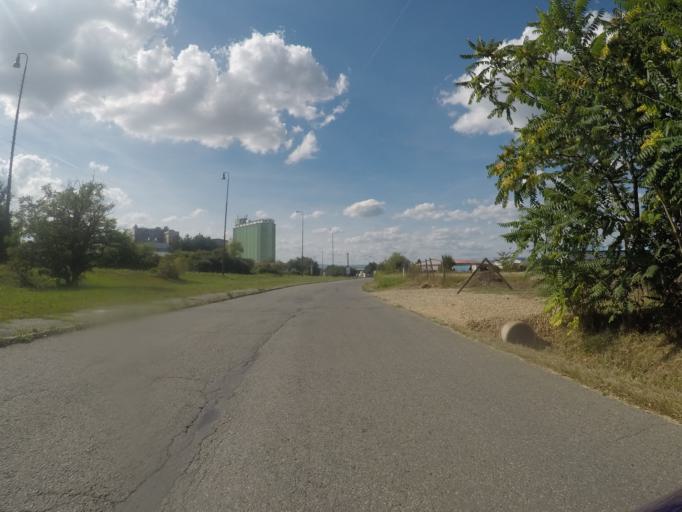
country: SK
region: Banskobystricky
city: Rimavska Sobota
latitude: 48.3899
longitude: 20.0094
